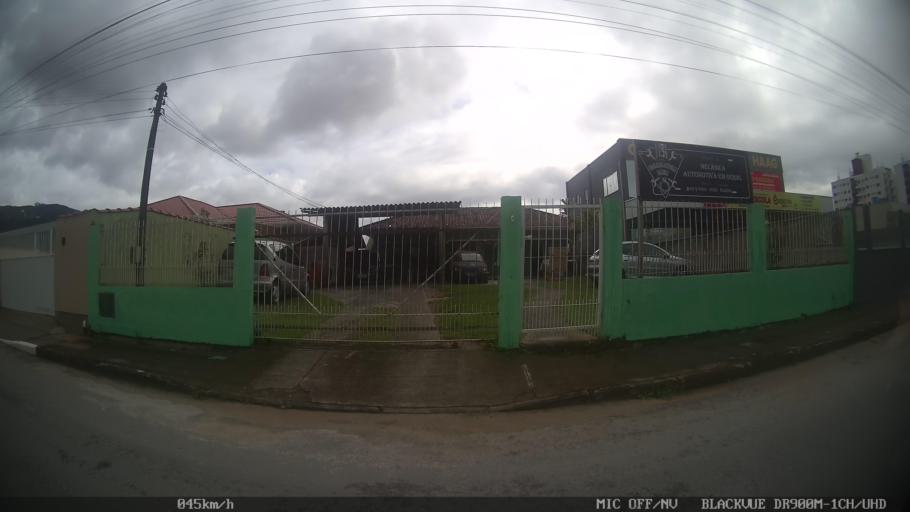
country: BR
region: Santa Catarina
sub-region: Biguacu
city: Biguacu
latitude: -27.5072
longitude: -48.6529
